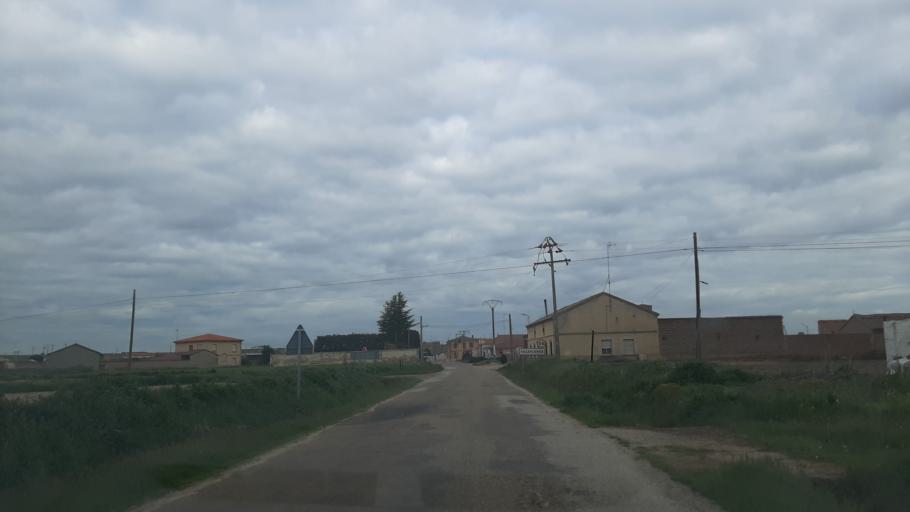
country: ES
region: Castille and Leon
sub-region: Provincia de Salamanca
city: Villaflores
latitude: 41.0828
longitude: -5.2283
